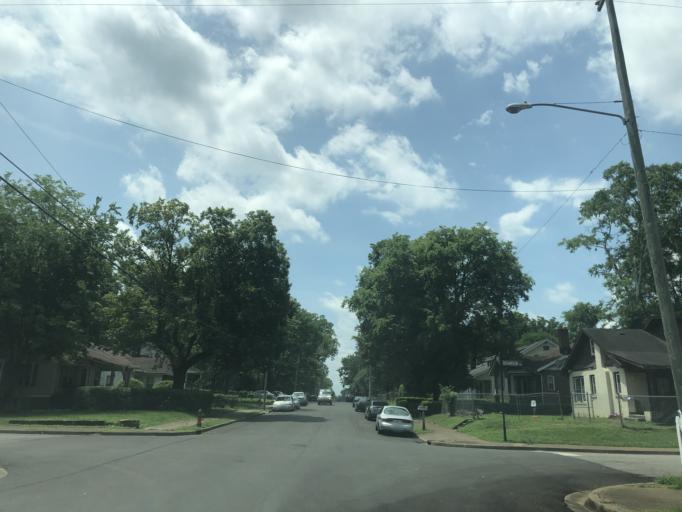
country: US
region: Tennessee
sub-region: Davidson County
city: Nashville
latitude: 36.1927
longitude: -86.7621
